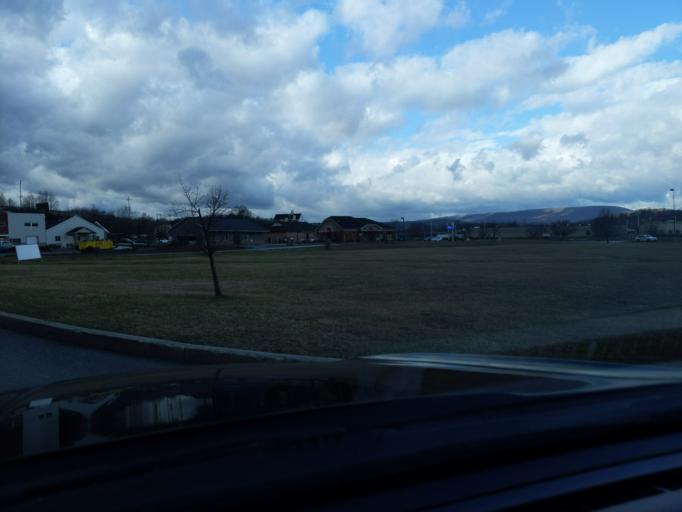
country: US
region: Pennsylvania
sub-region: Blair County
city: Hollidaysburg
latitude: 40.4309
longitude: -78.4116
